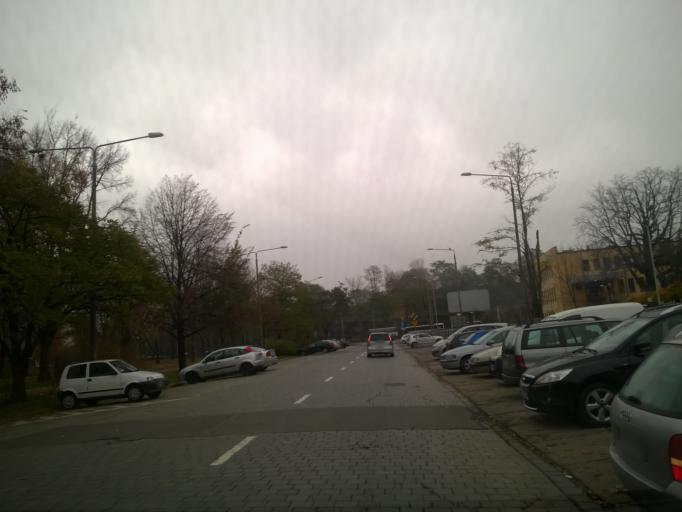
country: PL
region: Lower Silesian Voivodeship
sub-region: Powiat wroclawski
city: Wroclaw
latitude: 51.0913
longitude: 17.0274
